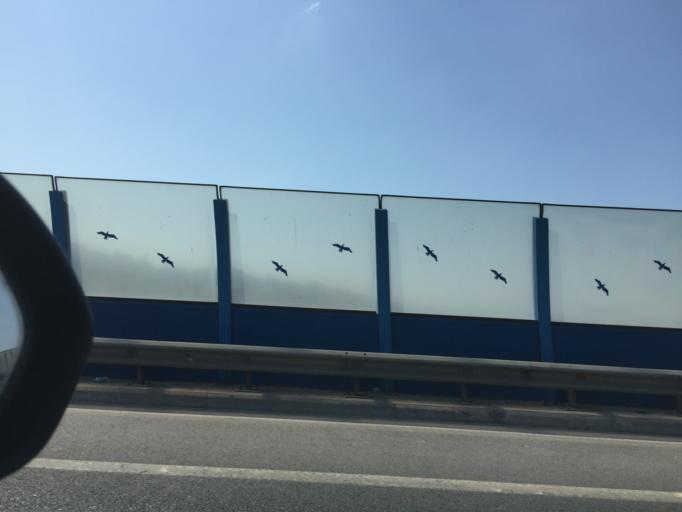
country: TR
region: Izmir
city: Karsiyaka
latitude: 38.4856
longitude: 27.1373
